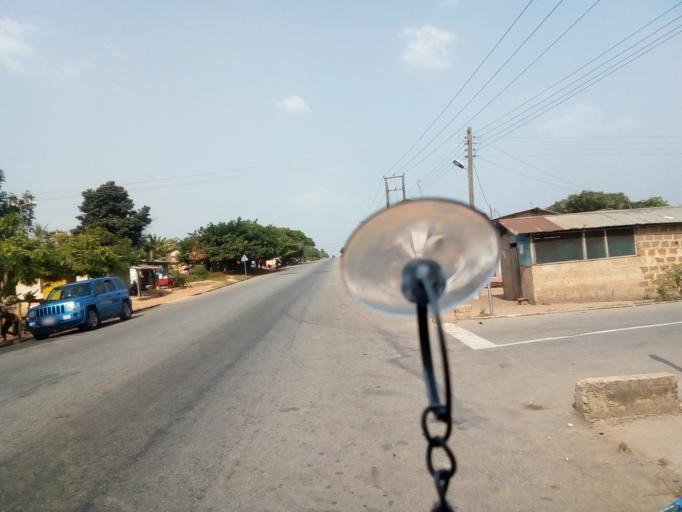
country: GH
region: Eastern
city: Suhum
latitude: 6.0656
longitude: -0.3987
